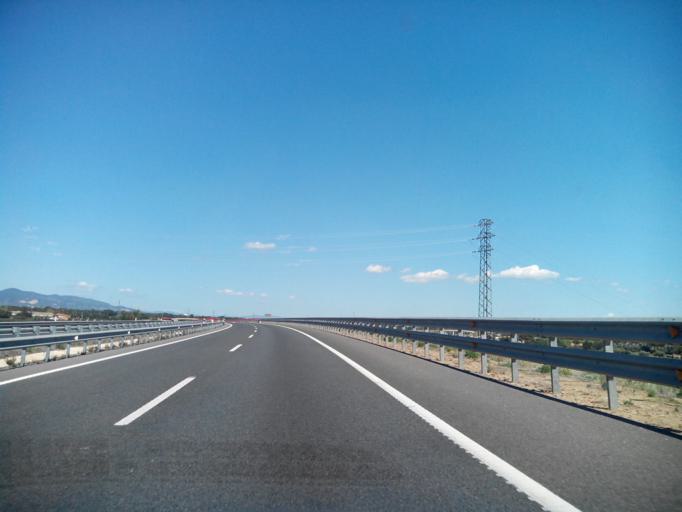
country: ES
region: Catalonia
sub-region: Provincia de Tarragona
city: Cambrils
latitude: 41.0683
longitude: 1.0104
